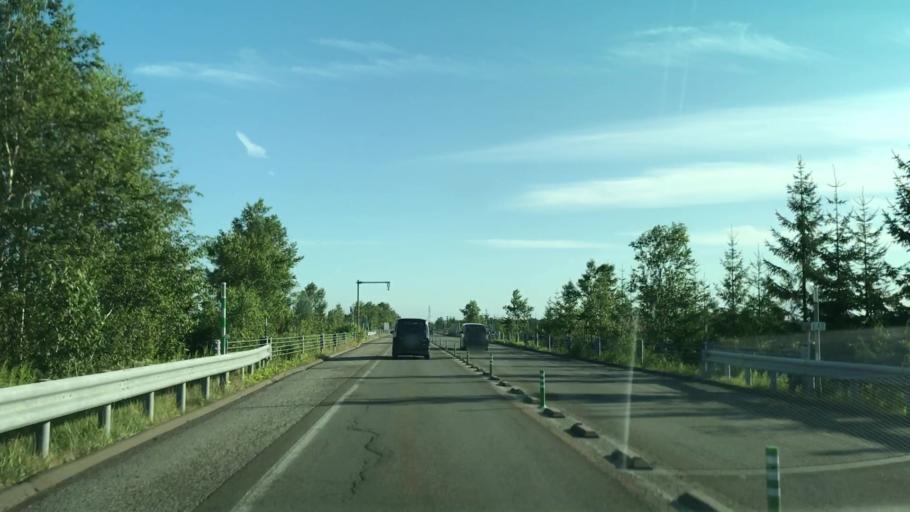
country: JP
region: Hokkaido
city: Chitose
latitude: 42.8742
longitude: 141.6155
